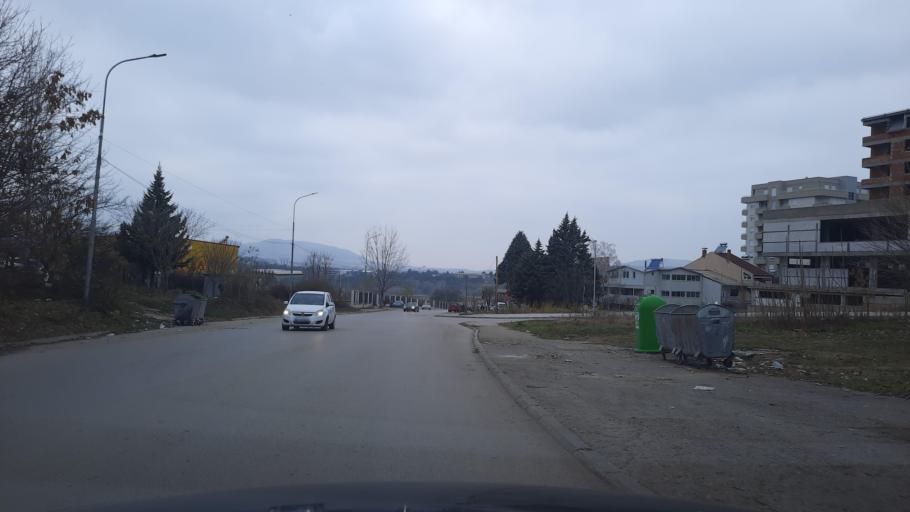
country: MK
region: Stip
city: Shtip
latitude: 41.7503
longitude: 22.1990
